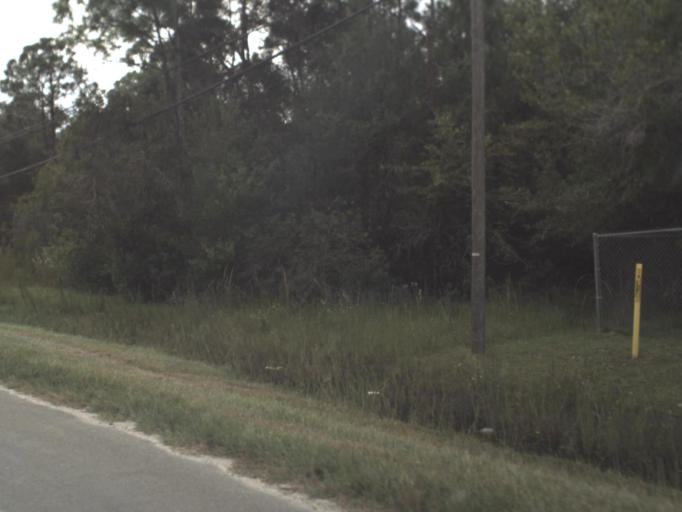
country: US
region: Florida
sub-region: Lee County
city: Fort Myers Shores
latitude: 26.7889
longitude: -81.7606
